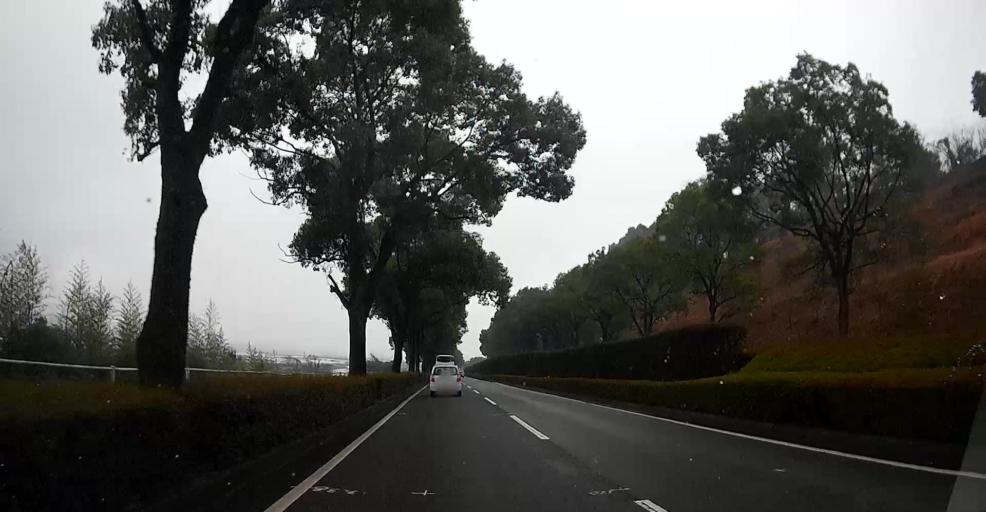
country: JP
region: Kumamoto
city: Ozu
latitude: 32.8175
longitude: 130.8419
